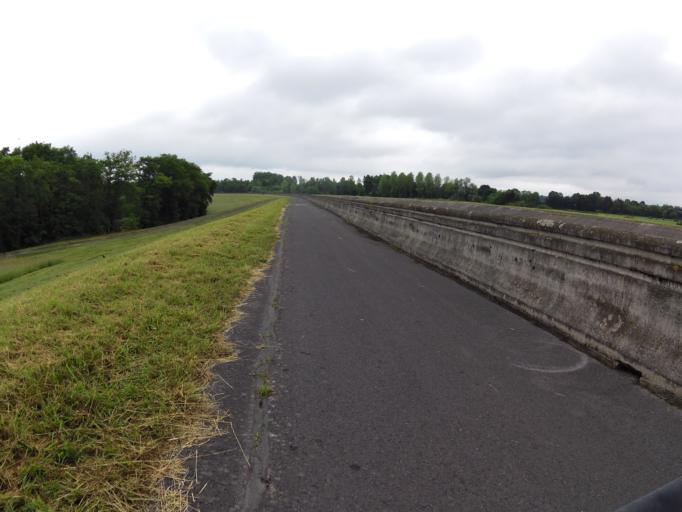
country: FR
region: Champagne-Ardenne
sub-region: Departement de la Haute-Marne
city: Villiers-en-Lieu
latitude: 48.5977
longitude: 4.8616
